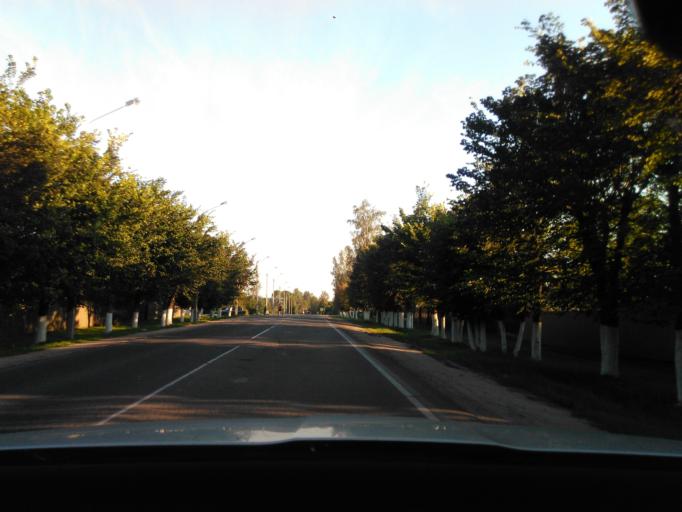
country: RU
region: Tverskaya
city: Konakovo
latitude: 56.6846
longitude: 36.7619
